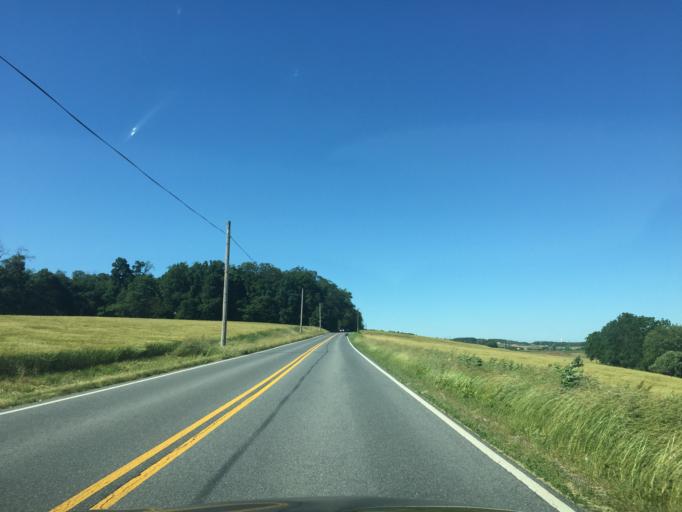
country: US
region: Maryland
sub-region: Carroll County
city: Hampstead
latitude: 39.6037
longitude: -76.9095
